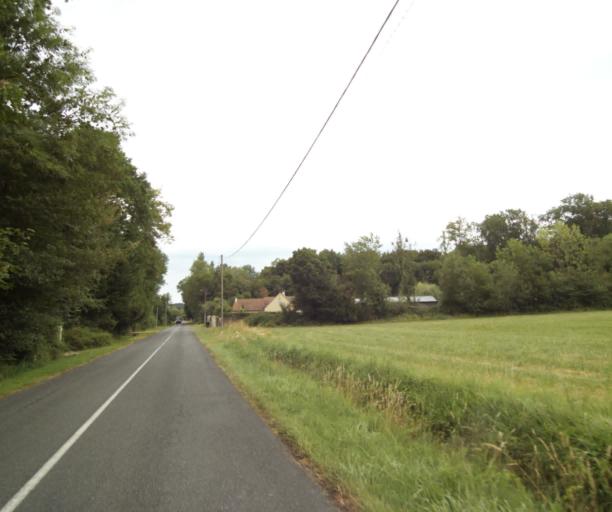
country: FR
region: Ile-de-France
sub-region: Departement de Seine-et-Marne
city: Cely
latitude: 48.4543
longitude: 2.5422
